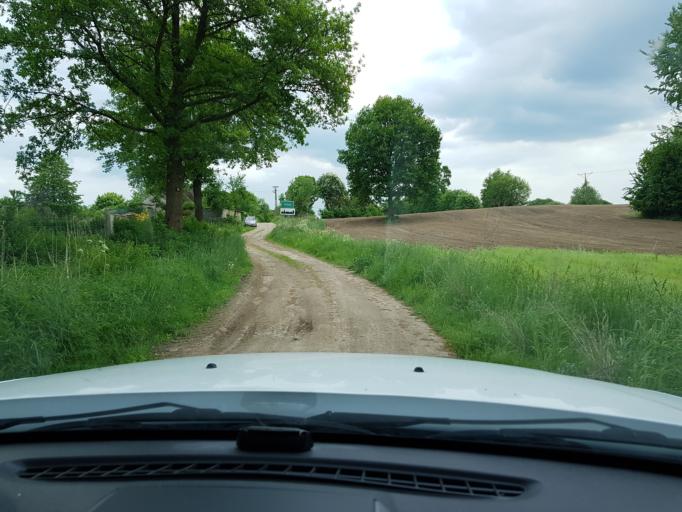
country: PL
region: West Pomeranian Voivodeship
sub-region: Powiat drawski
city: Drawsko Pomorskie
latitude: 53.5487
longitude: 15.7339
